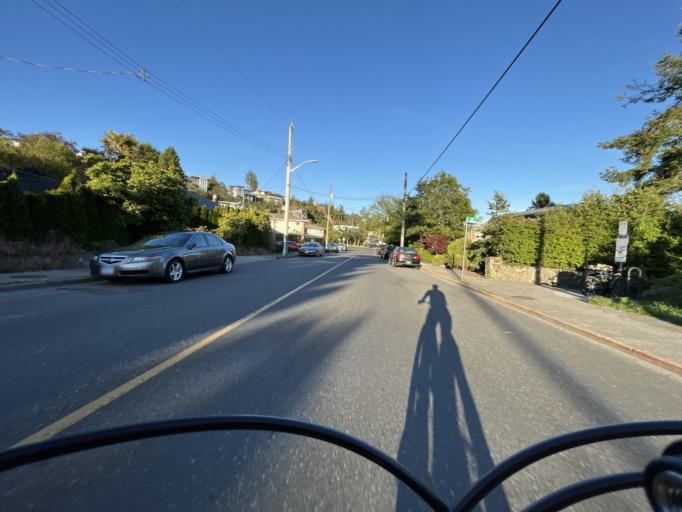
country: CA
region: British Columbia
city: Oak Bay
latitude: 48.4122
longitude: -123.3281
